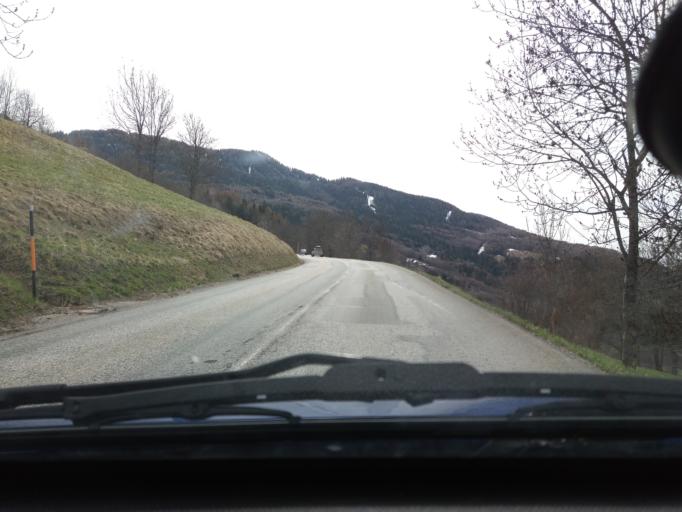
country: FR
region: Rhone-Alpes
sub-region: Departement de la Savoie
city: Macot-la-Plagne
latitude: 45.5436
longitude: 6.6719
